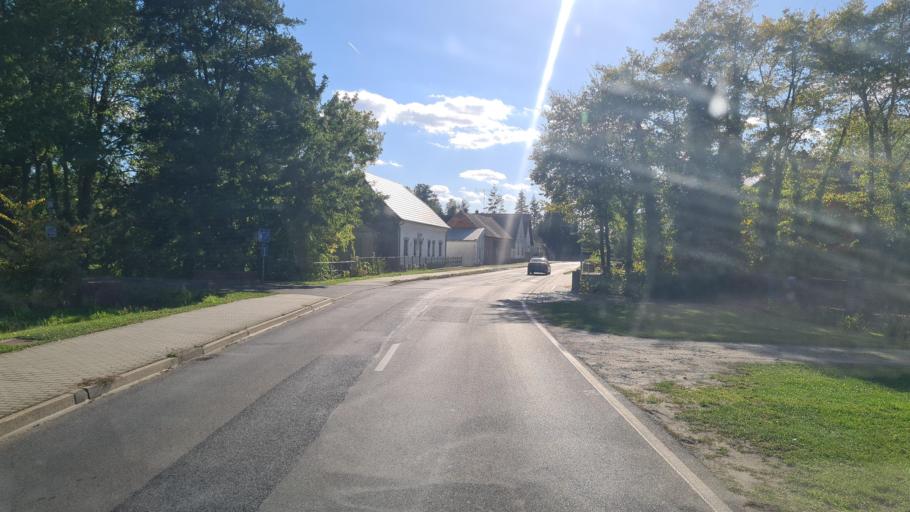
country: DE
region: Brandenburg
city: Kolkwitz
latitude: 51.7534
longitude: 14.2487
